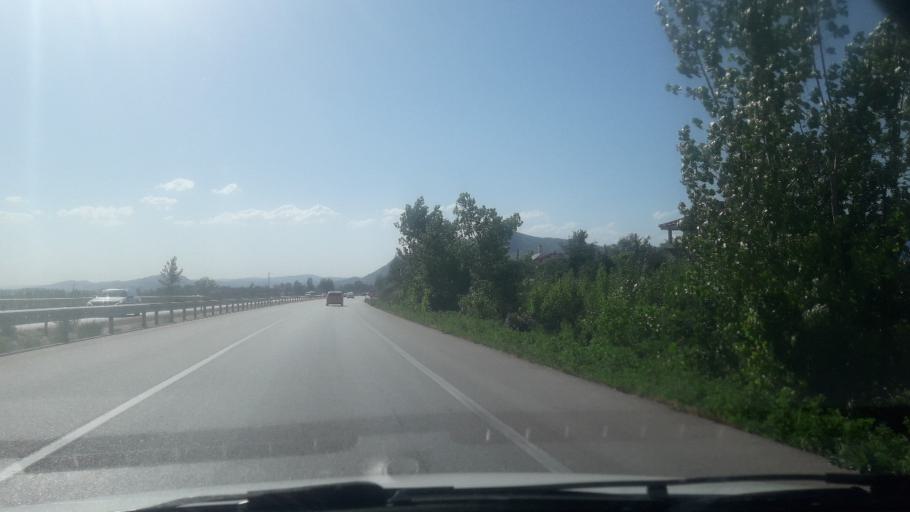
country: TR
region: Tokat
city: Dokmetepe
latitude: 40.3141
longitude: 36.2579
